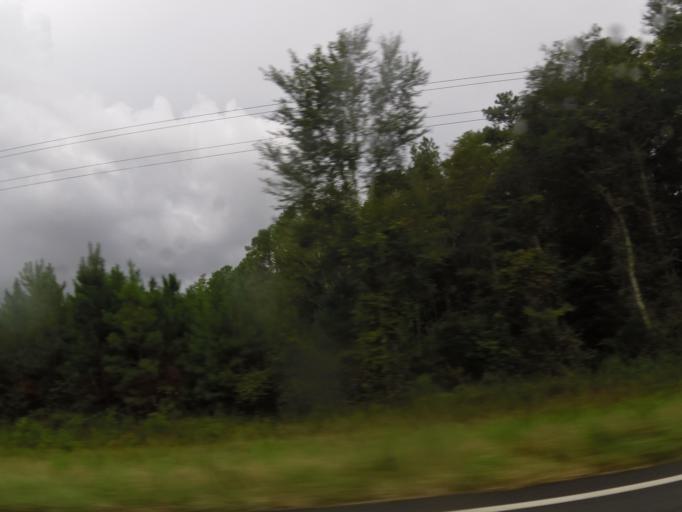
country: US
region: Florida
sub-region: Baker County
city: Macclenny
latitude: 30.3807
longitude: -82.1672
